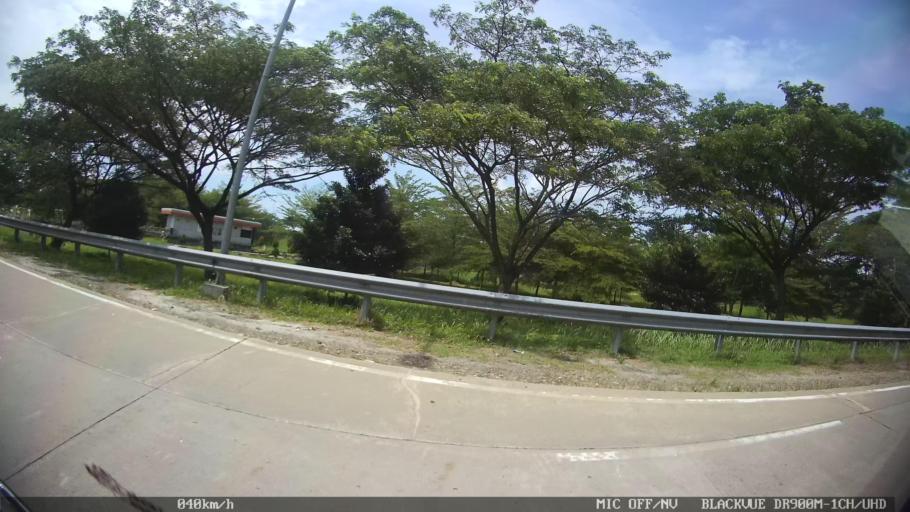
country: ID
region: North Sumatra
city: Percut
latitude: 3.6340
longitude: 98.8770
